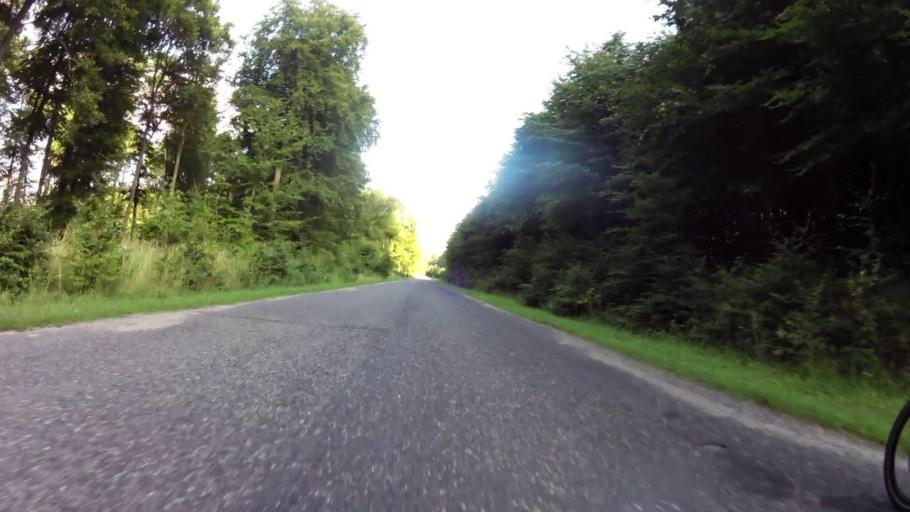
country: PL
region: West Pomeranian Voivodeship
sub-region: Powiat drawski
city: Drawsko Pomorskie
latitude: 53.4723
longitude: 15.8286
